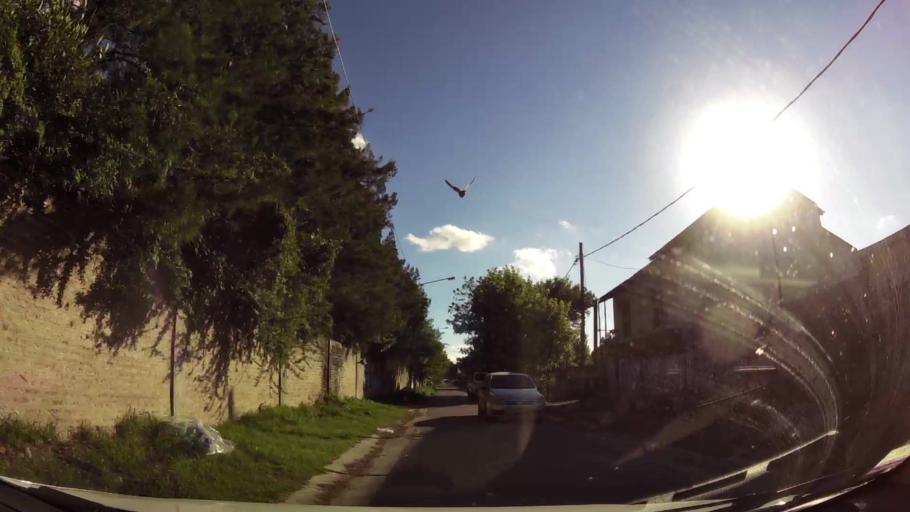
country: AR
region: Buenos Aires
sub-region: Partido de Moron
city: Moron
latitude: -34.6797
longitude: -58.6197
